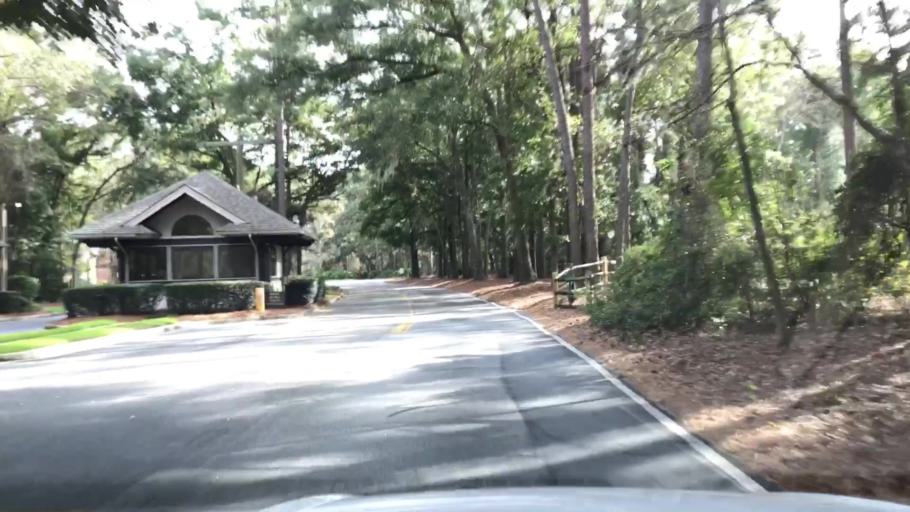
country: US
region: South Carolina
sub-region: Beaufort County
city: Hilton Head Island
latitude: 32.2185
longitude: -80.7237
